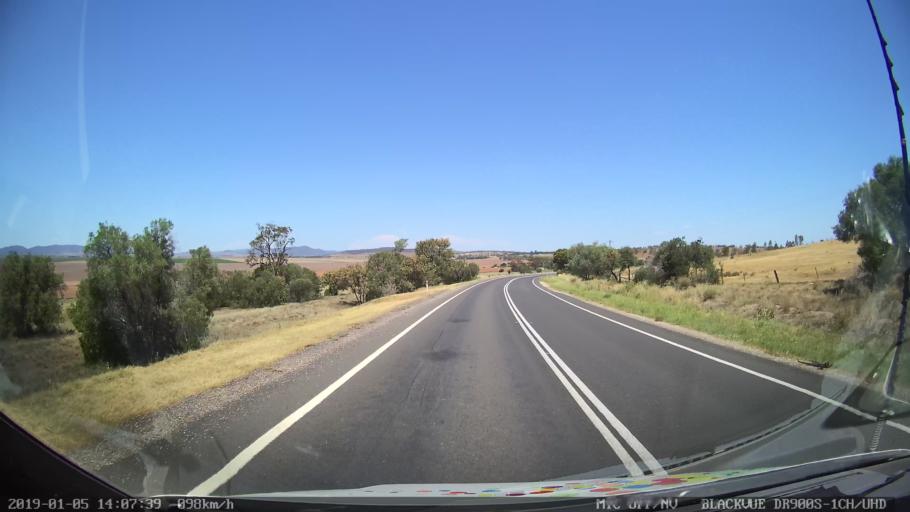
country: AU
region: New South Wales
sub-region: Gunnedah
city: Gunnedah
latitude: -31.2247
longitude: 150.4094
